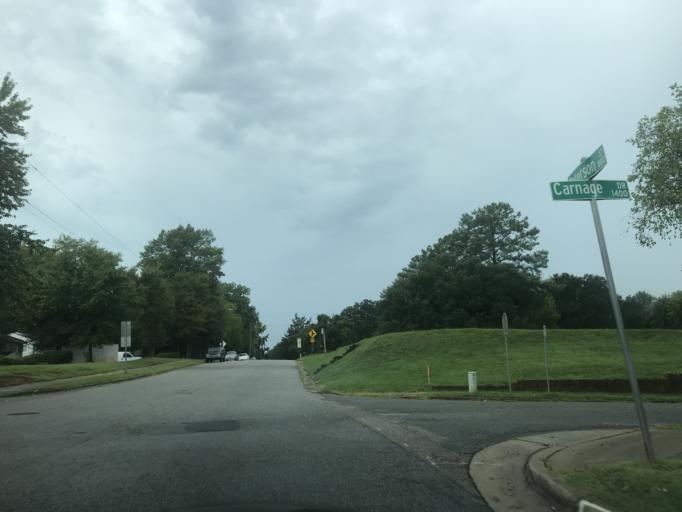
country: US
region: North Carolina
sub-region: Wake County
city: Raleigh
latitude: 35.7604
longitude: -78.6286
